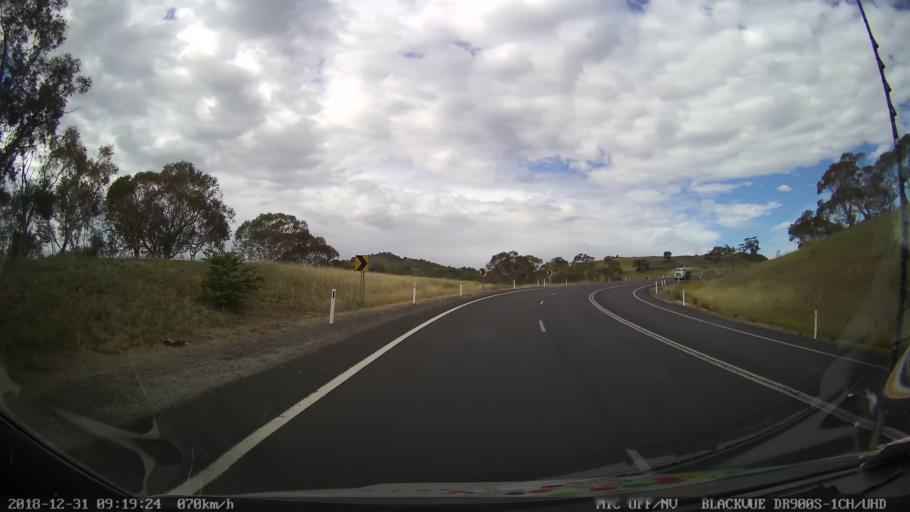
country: AU
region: New South Wales
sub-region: Snowy River
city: Jindabyne
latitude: -36.4151
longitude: 148.5862
